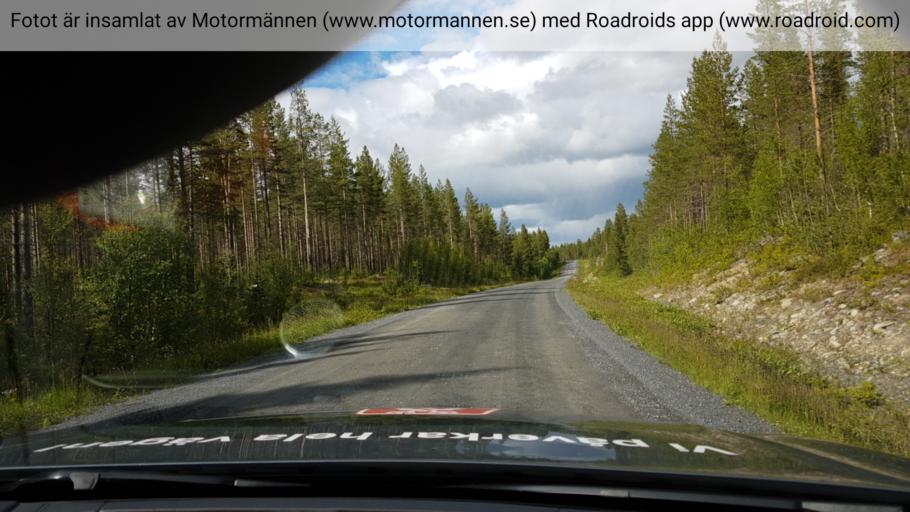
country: SE
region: Jaemtland
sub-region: Krokoms Kommun
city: Valla
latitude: 63.0717
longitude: 13.9586
